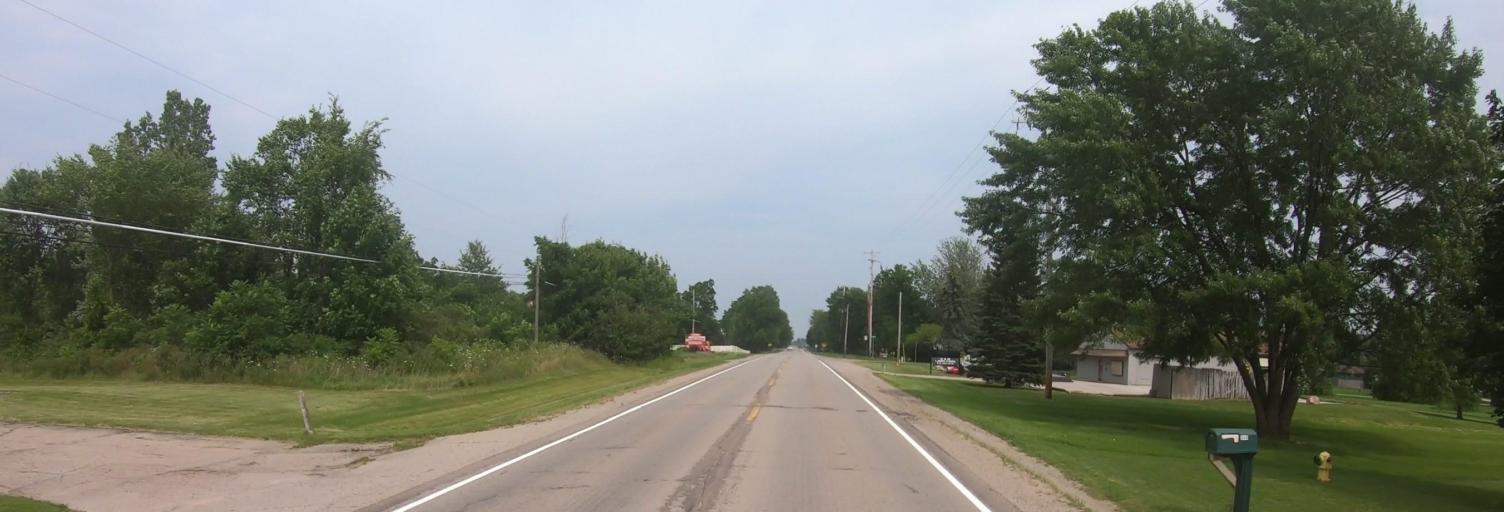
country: US
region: Michigan
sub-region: Genesee County
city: Swartz Creek
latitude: 42.9570
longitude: -83.8668
